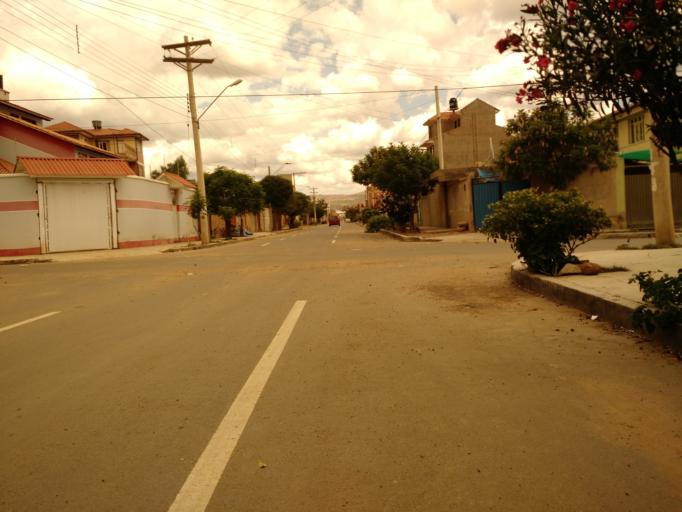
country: BO
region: Cochabamba
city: Cochabamba
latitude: -17.4255
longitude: -66.1246
